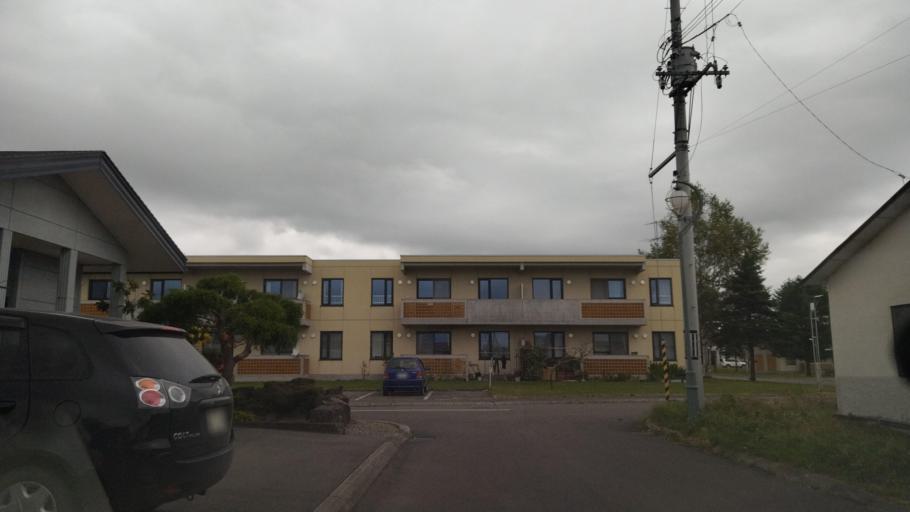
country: JP
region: Hokkaido
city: Otofuke
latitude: 43.2302
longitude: 143.2976
